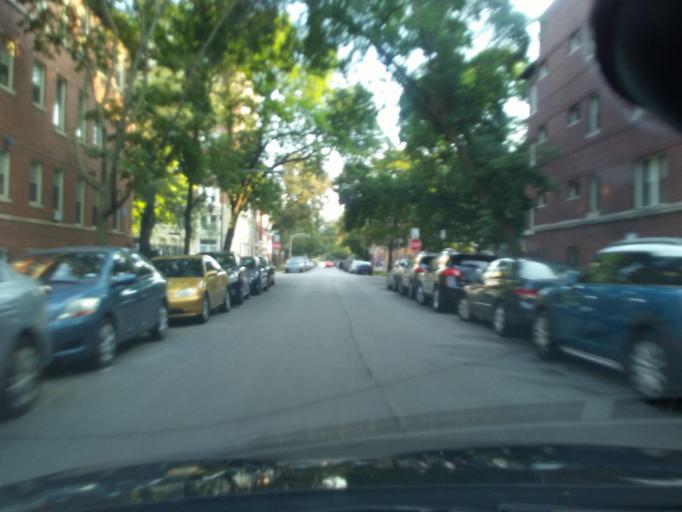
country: US
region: Illinois
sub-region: Cook County
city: Evanston
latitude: 42.0167
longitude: -87.6681
